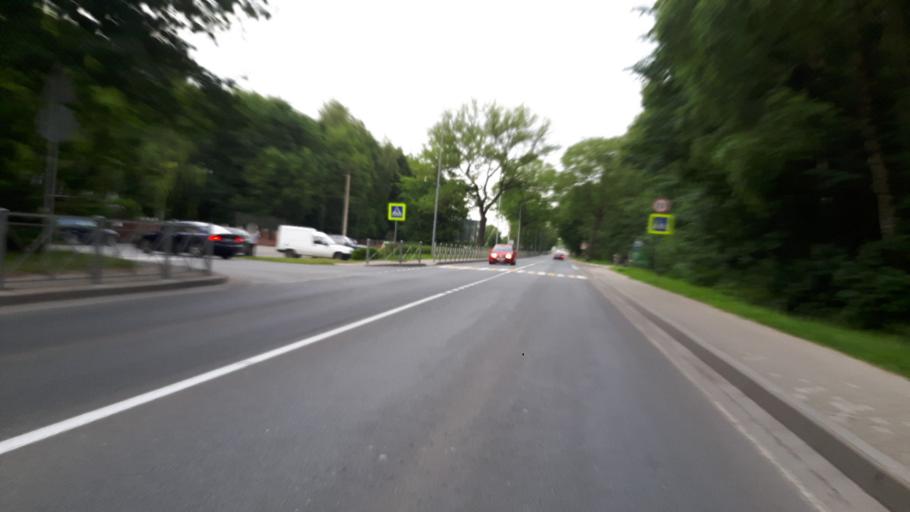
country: RU
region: Kaliningrad
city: Vzmorye
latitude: 54.6464
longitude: 20.3572
